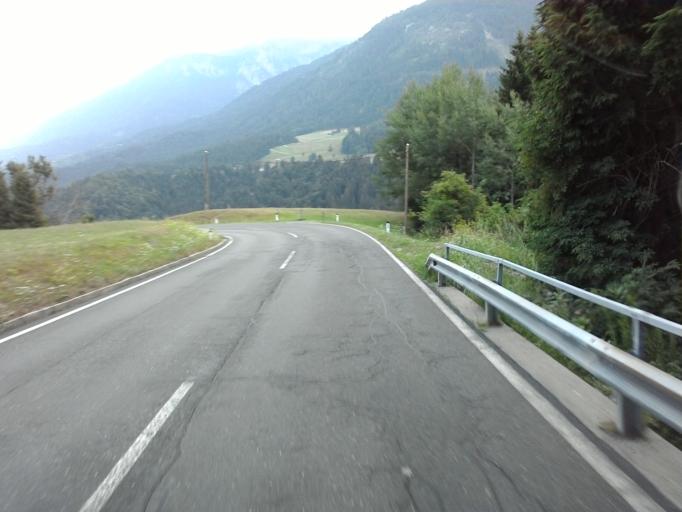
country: AT
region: Carinthia
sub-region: Politischer Bezirk Spittal an der Drau
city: Oberdrauburg
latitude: 46.6840
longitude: 12.9416
